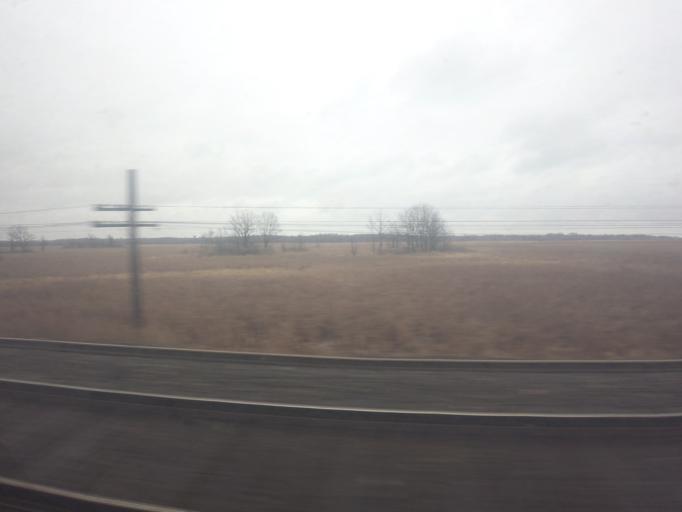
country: CA
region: Ontario
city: Kingston
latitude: 44.2763
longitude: -76.4717
